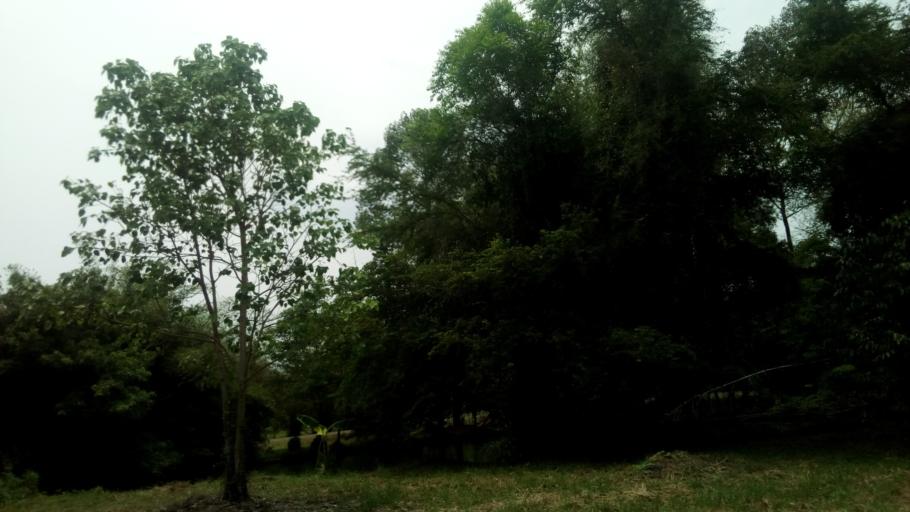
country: TH
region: Bangkok
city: Thawi Watthana
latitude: 13.7821
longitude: 100.3131
